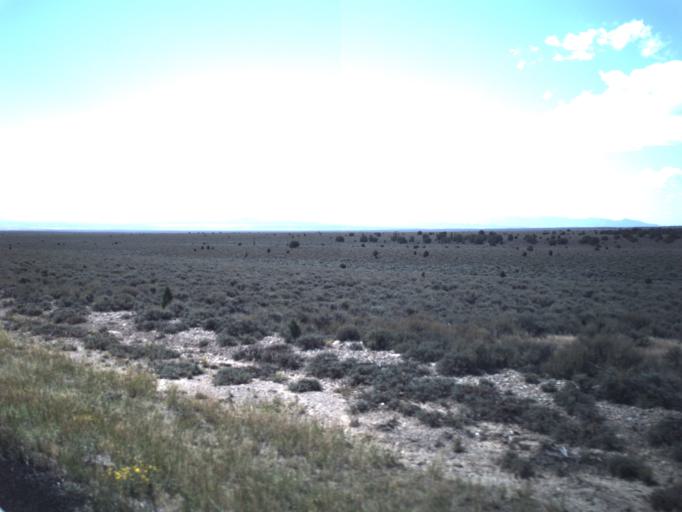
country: US
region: Utah
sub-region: Iron County
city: Parowan
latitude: 38.0174
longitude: -112.9981
